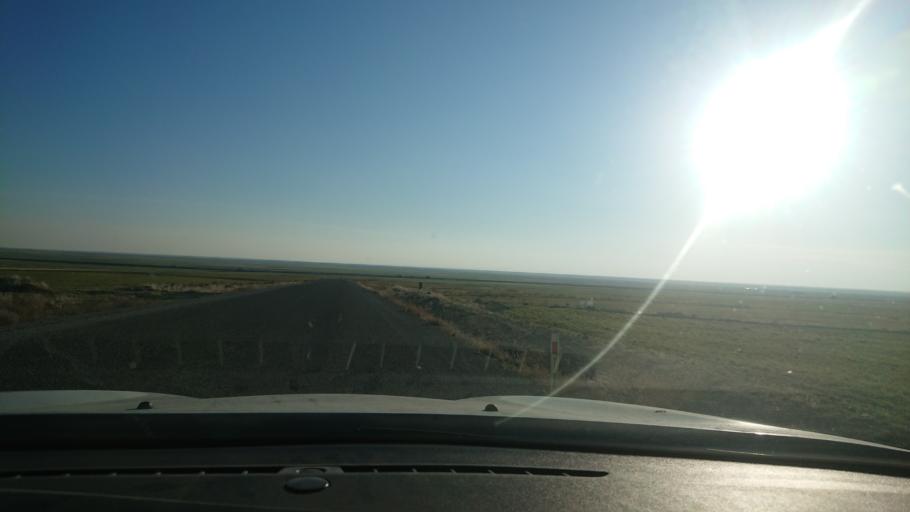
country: TR
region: Aksaray
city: Acipinar
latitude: 38.6710
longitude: 33.7262
